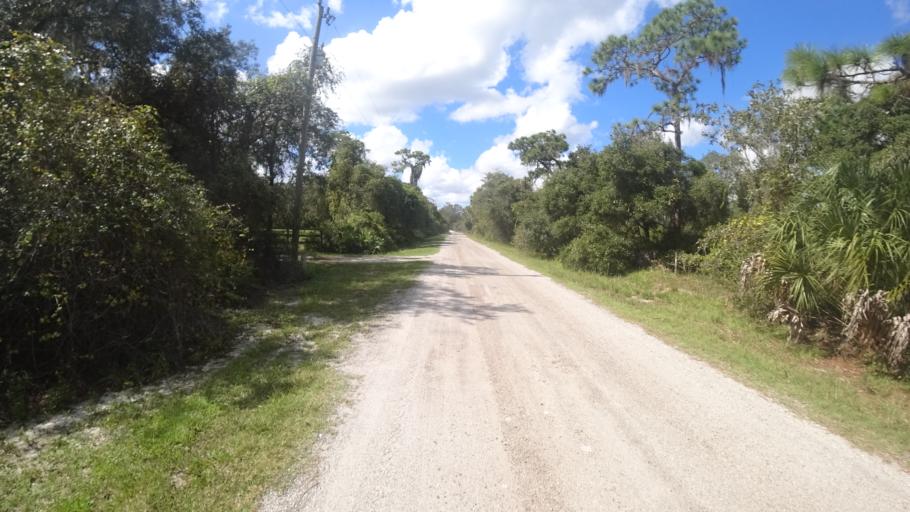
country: US
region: Florida
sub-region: Sarasota County
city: Lake Sarasota
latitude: 27.3204
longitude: -82.2537
